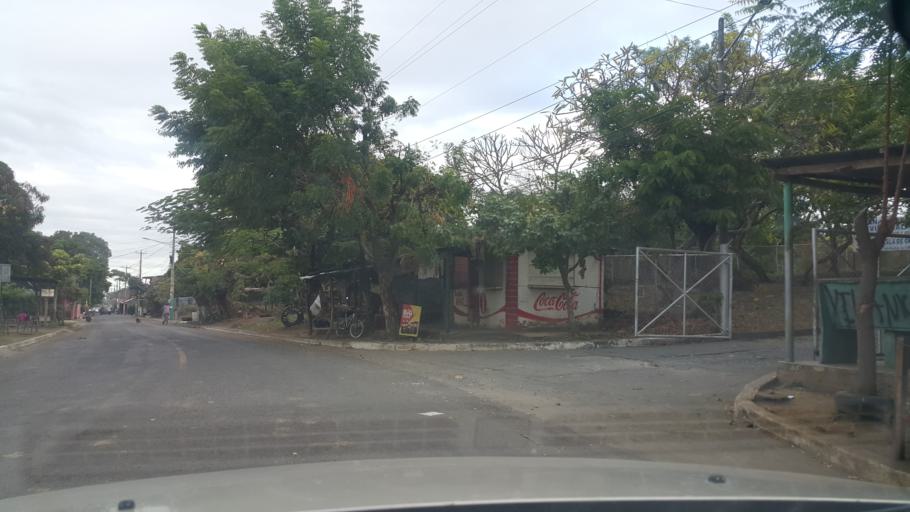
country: NI
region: Rivas
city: Moyogalpa
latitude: 11.5360
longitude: -85.6963
